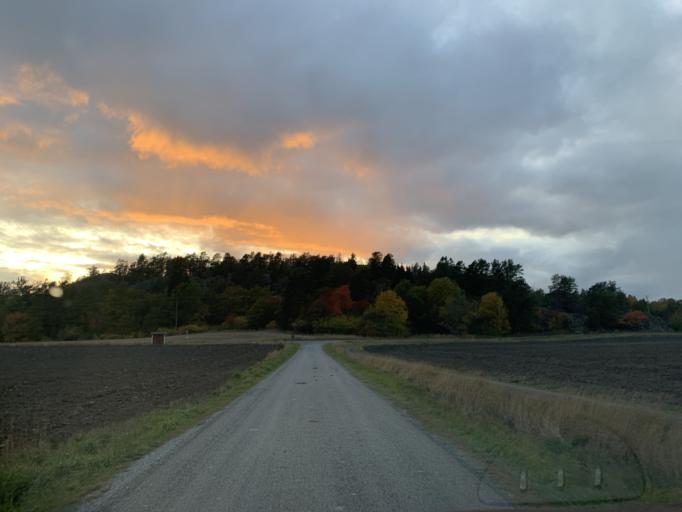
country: SE
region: Stockholm
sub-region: Nynashamns Kommun
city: Osmo
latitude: 58.8999
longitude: 17.7951
